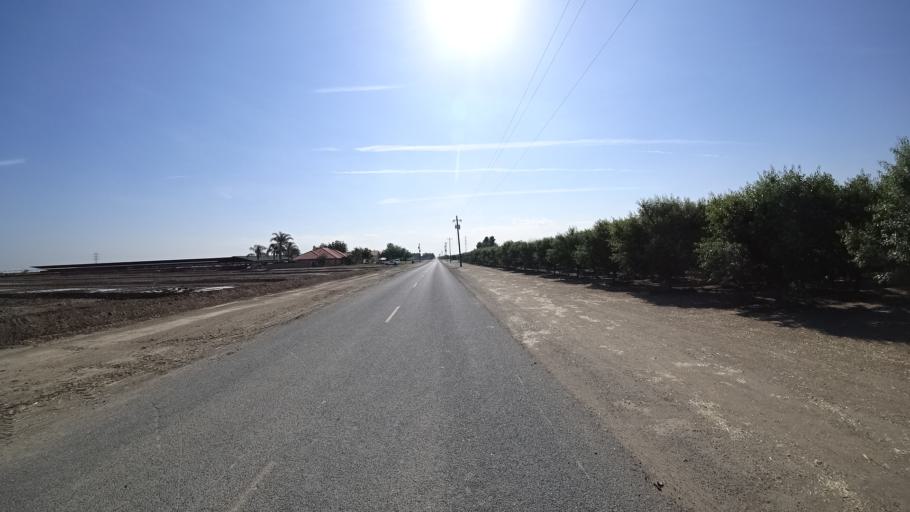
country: US
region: California
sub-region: Kings County
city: Home Garden
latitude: 36.2259
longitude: -119.5964
